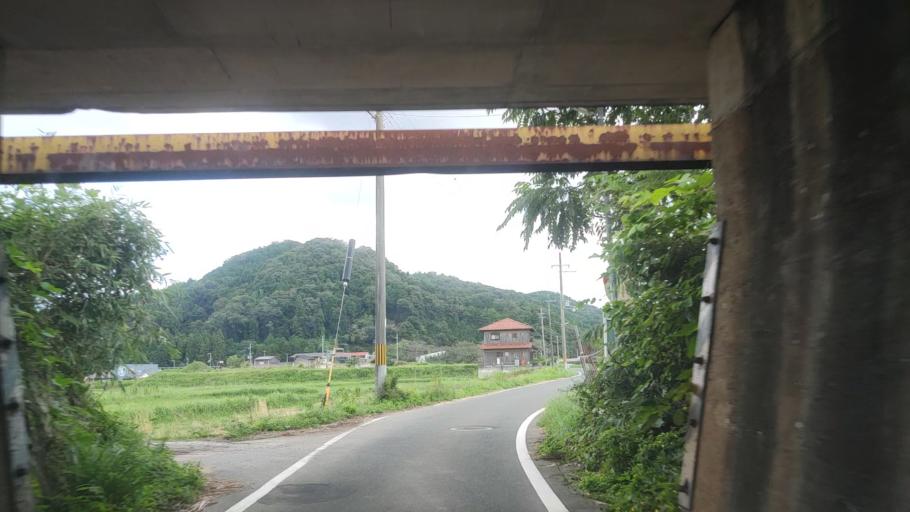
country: JP
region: Hyogo
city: Toyooka
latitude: 35.5978
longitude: 134.8848
